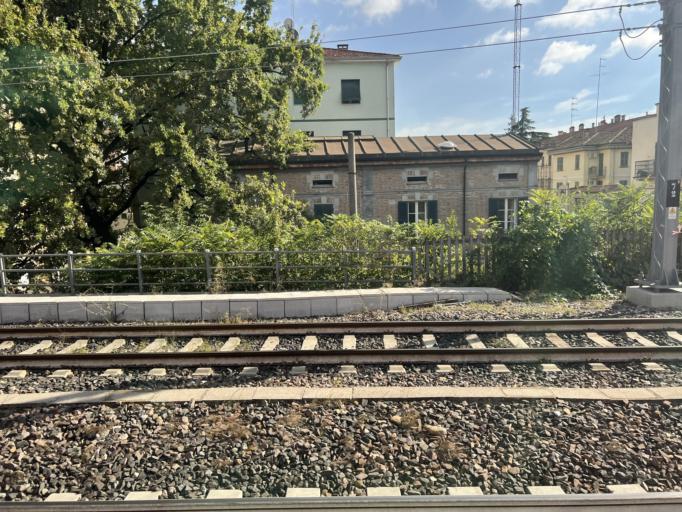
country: IT
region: Emilia-Romagna
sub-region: Provincia di Parma
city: Parma
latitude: 44.8111
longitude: 10.3241
